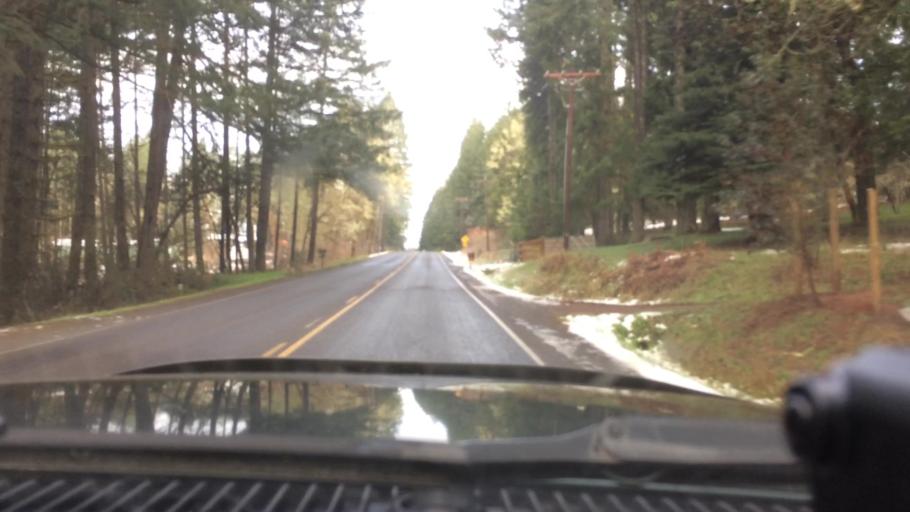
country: US
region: Oregon
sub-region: Lane County
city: Veneta
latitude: 44.1358
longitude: -123.3524
